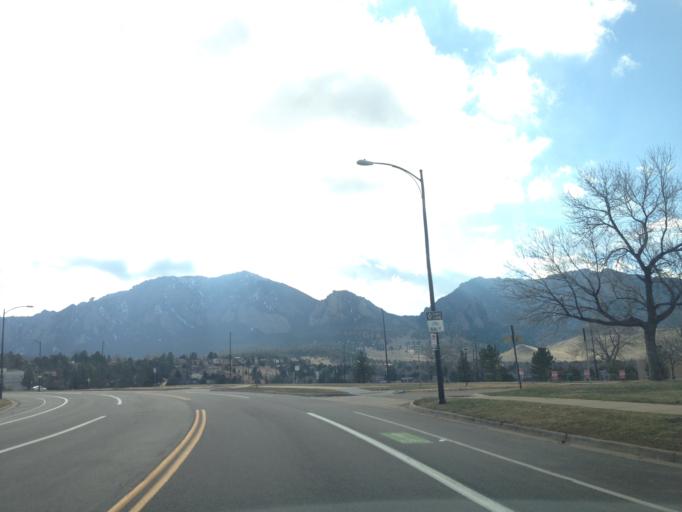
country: US
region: Colorado
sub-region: Boulder County
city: Boulder
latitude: 39.9715
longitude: -105.2454
